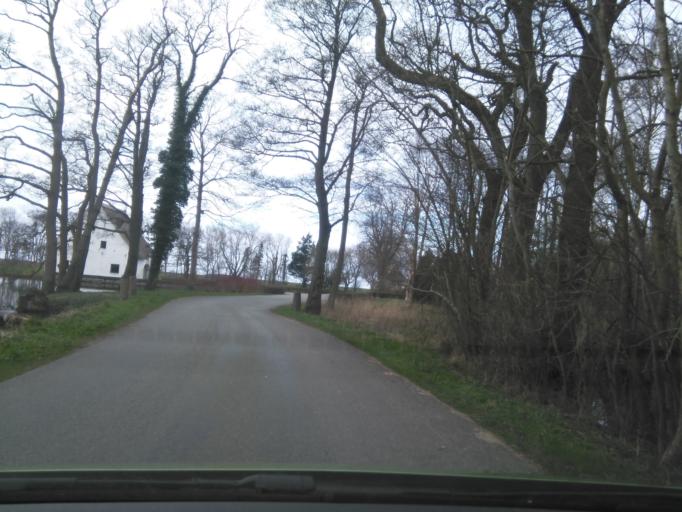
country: DK
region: South Denmark
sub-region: Nordfyns Kommune
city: Bogense
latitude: 55.5639
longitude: 10.1471
